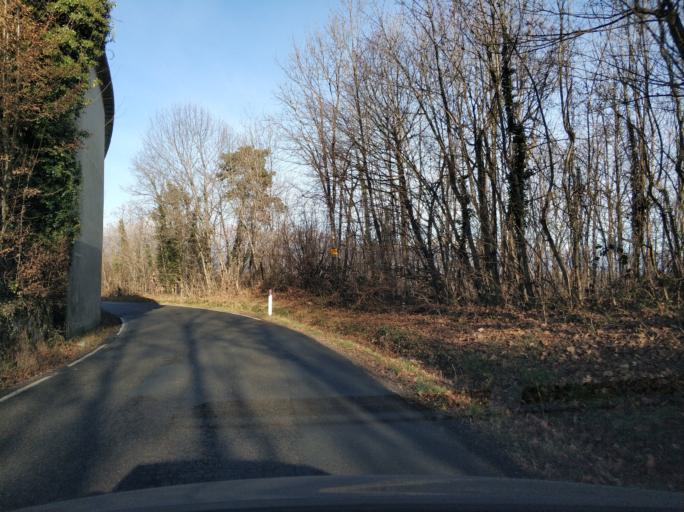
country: IT
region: Piedmont
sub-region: Provincia di Torino
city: Robassomero
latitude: 45.2101
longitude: 7.5524
